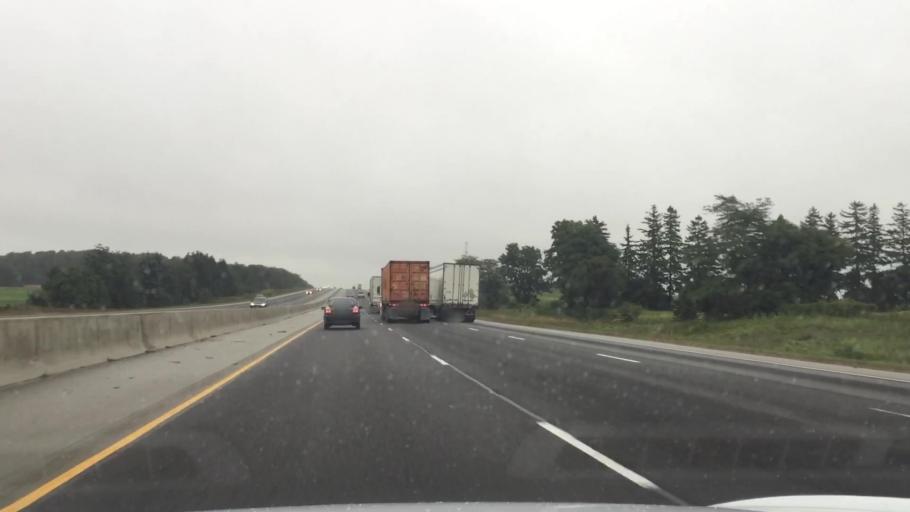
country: CA
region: Ontario
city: Kitchener
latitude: 43.2829
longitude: -80.5160
